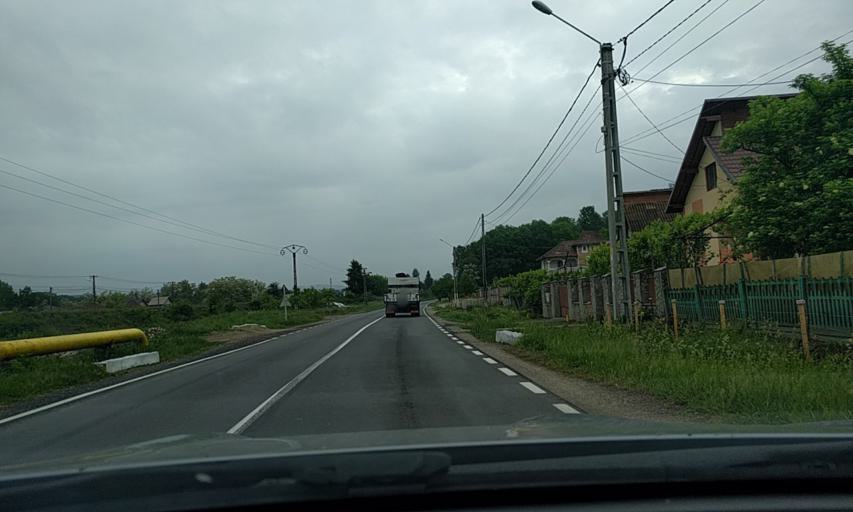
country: RO
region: Dambovita
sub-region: Comuna Vulcana-Pandele
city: Vulcana-Pandele
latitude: 45.0127
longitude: 25.4051
